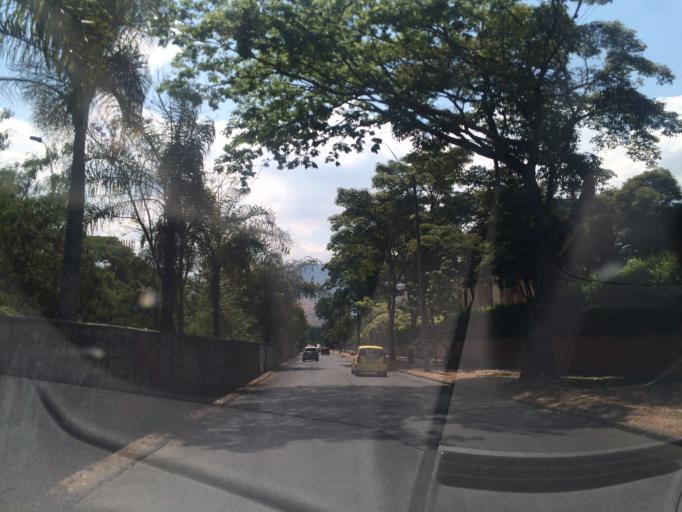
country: CO
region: Valle del Cauca
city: Cali
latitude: 3.4821
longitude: -76.5107
